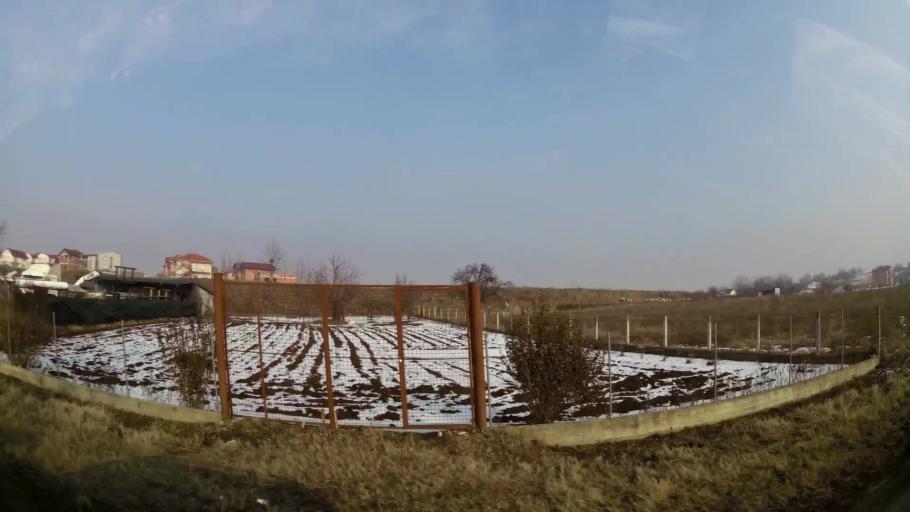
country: MK
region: Ilinden
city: Marino
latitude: 41.9832
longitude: 21.5954
